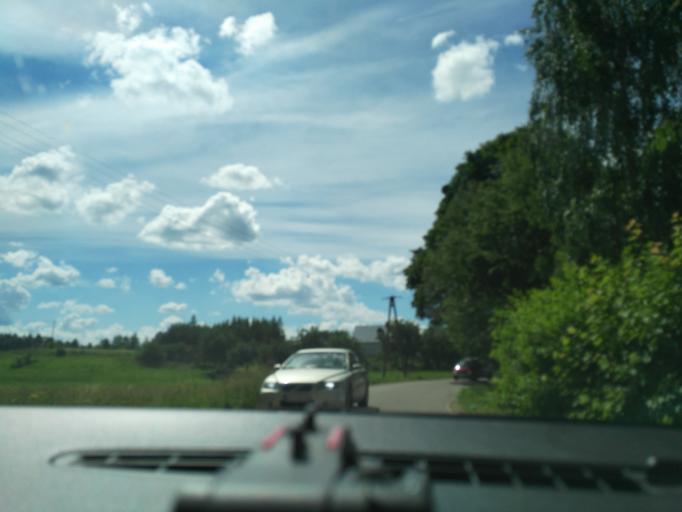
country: PL
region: Podlasie
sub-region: Powiat sejnenski
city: Sejny
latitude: 54.0304
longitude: 23.3198
